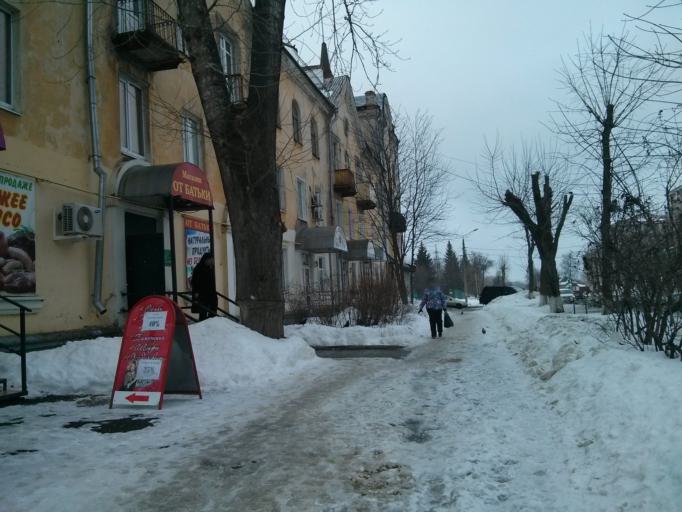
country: RU
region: Vladimir
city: Murom
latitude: 55.5556
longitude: 42.0608
